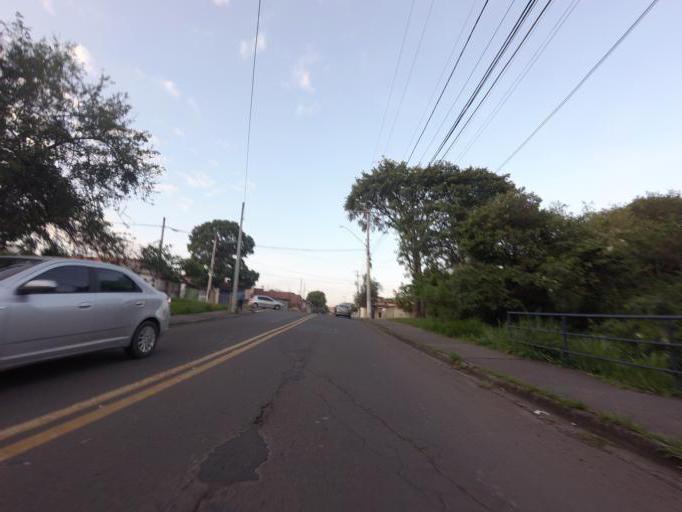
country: BR
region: Sao Paulo
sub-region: Piracicaba
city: Piracicaba
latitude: -22.7564
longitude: -47.6085
